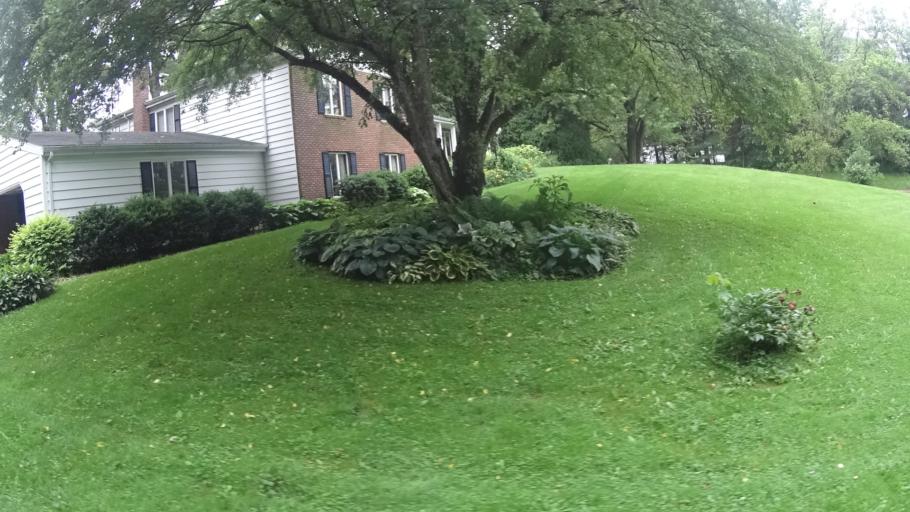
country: US
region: Ohio
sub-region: Erie County
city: Huron
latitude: 41.3567
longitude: -82.5849
